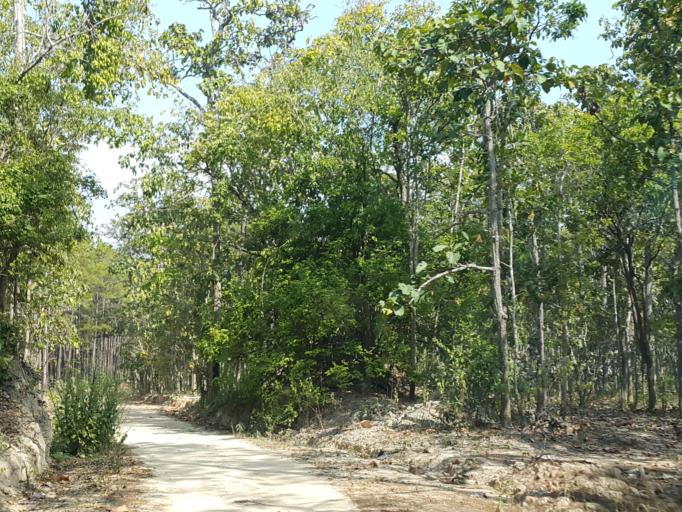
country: TH
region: Chiang Mai
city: Hot
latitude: 18.1386
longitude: 98.4268
